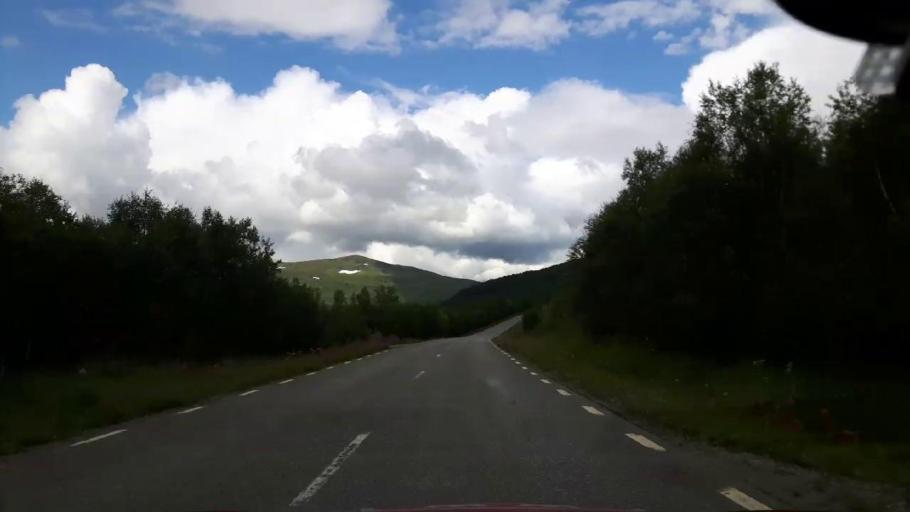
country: NO
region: Nordland
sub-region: Hattfjelldal
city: Hattfjelldal
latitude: 65.0628
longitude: 14.6996
